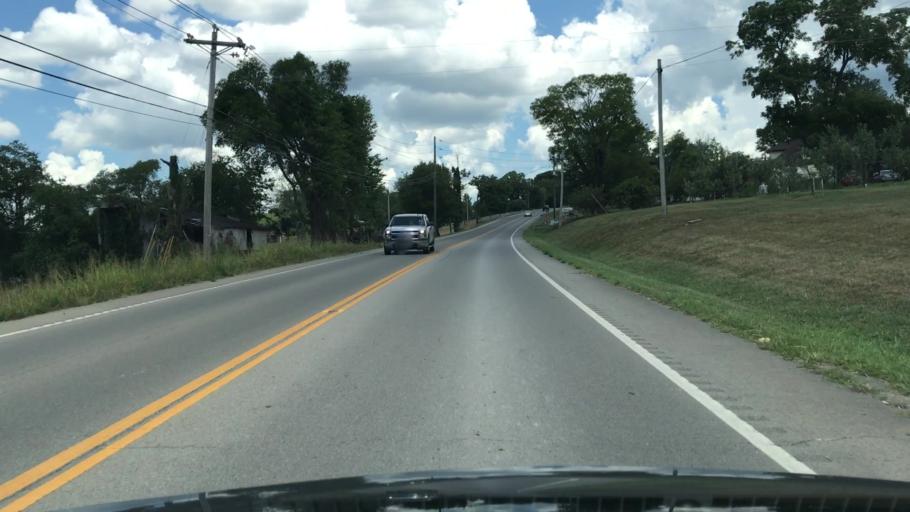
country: US
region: Tennessee
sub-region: Williamson County
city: Nolensville
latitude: 35.8946
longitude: -86.6661
